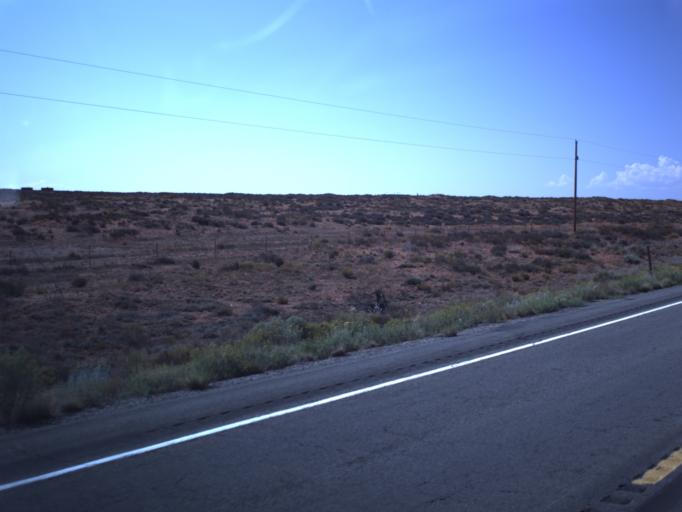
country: US
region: Utah
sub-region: San Juan County
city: Blanding
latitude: 37.0281
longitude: -109.5988
